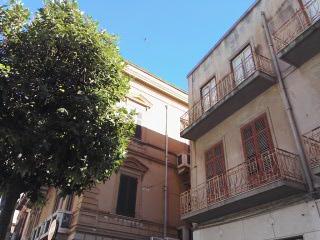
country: IT
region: Sicily
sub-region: Trapani
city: Marsala
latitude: 37.7973
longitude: 12.4384
